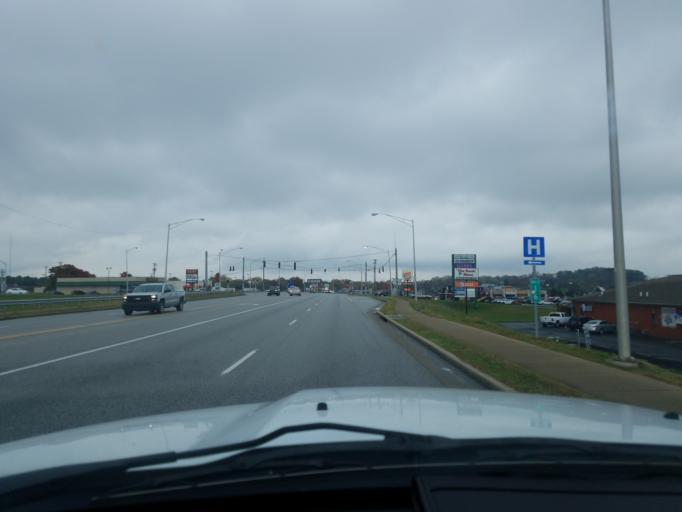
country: US
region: Kentucky
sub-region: Taylor County
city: Campbellsville
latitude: 37.3439
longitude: -85.3667
